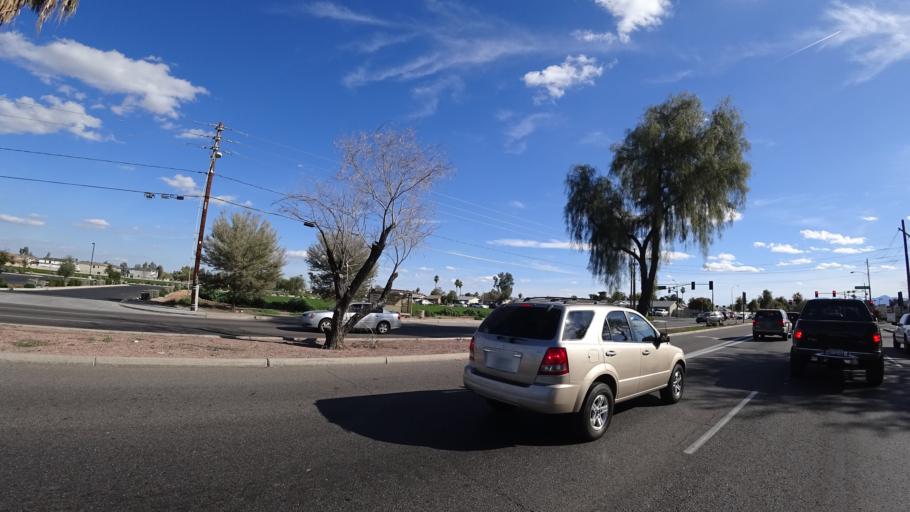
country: US
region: Arizona
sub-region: Maricopa County
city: Tolleson
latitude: 33.4736
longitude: -112.2209
